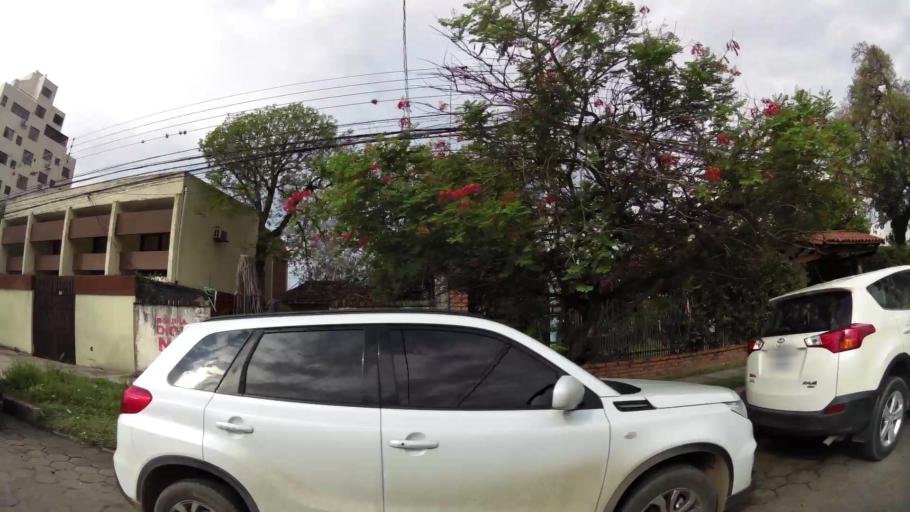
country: BO
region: Santa Cruz
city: Santa Cruz de la Sierra
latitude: -17.7898
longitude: -63.1770
